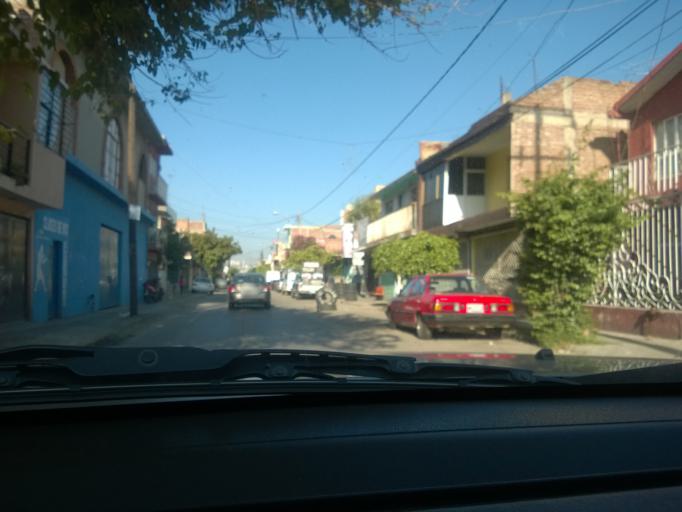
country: MX
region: Guanajuato
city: Leon
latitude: 21.1461
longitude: -101.6667
